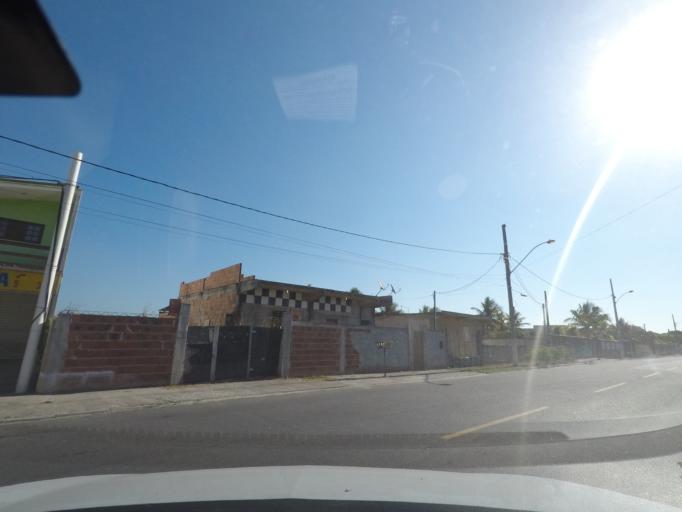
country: BR
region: Rio de Janeiro
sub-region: Marica
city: Marica
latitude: -22.9701
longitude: -42.9127
